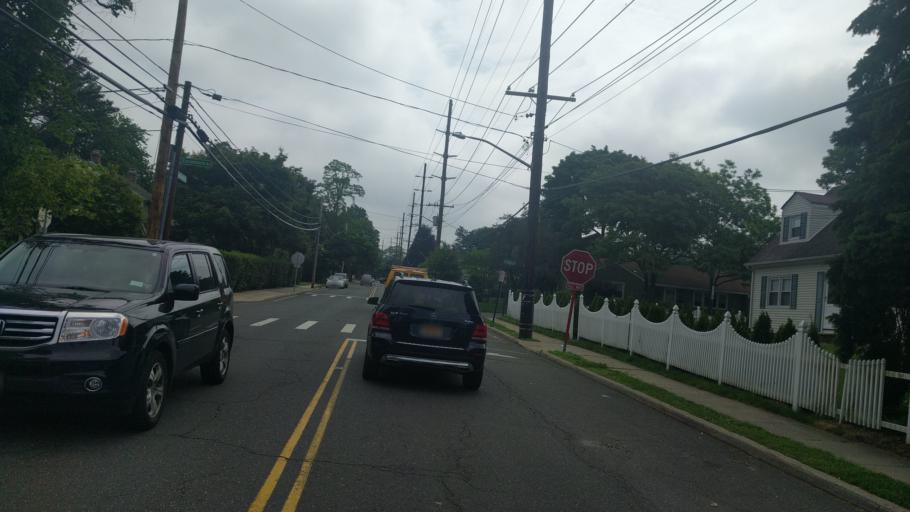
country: US
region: New York
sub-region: Nassau County
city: Glenwood Landing
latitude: 40.8310
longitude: -73.6377
